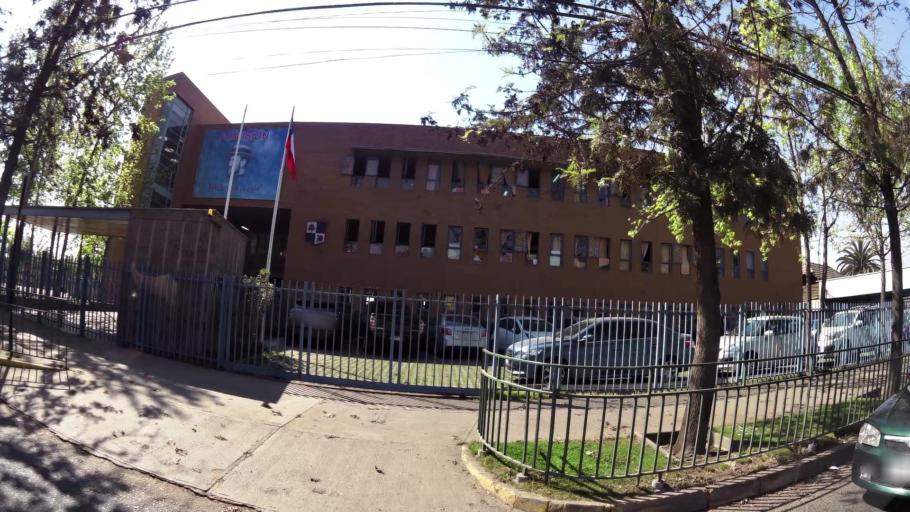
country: CL
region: Santiago Metropolitan
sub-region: Provincia de Santiago
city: La Pintana
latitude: -33.5394
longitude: -70.5965
